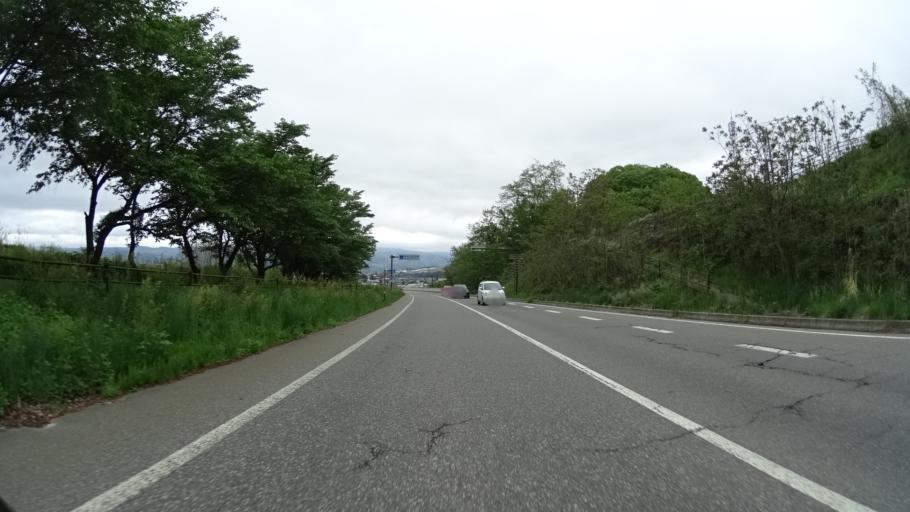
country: JP
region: Nagano
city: Nakano
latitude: 36.7544
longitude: 138.3955
